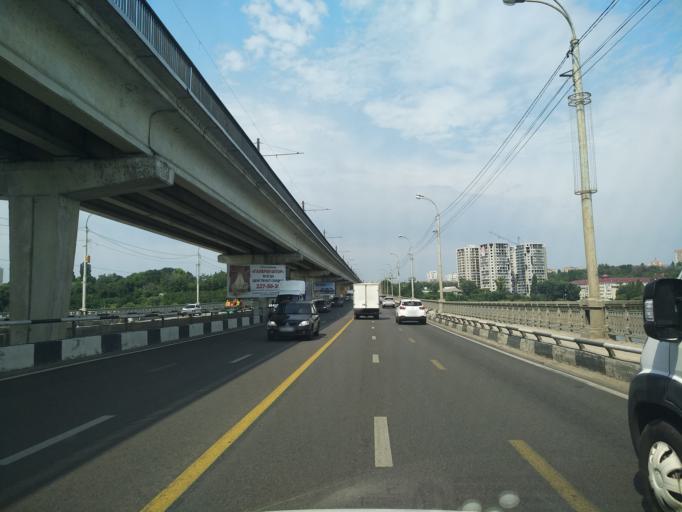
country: RU
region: Voronezj
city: Voronezh
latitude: 51.6923
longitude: 39.2390
